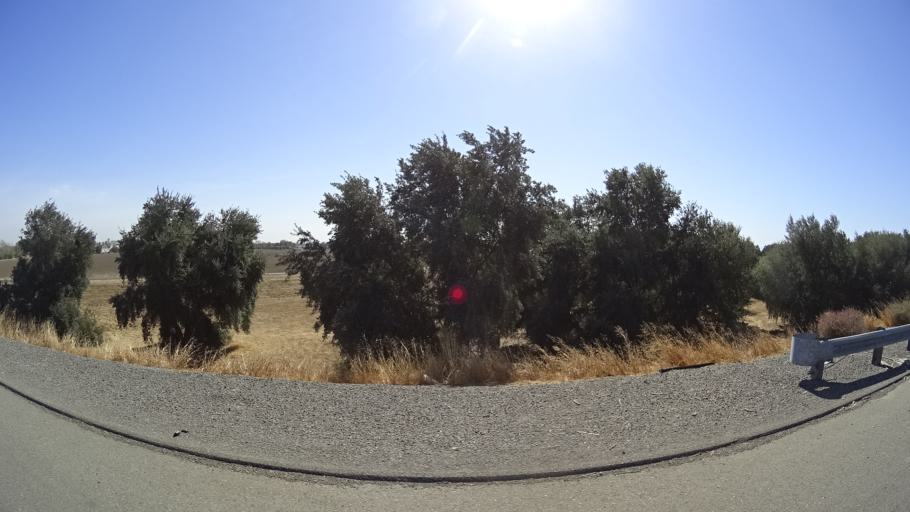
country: US
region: California
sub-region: Yolo County
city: Woodland
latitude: 38.6193
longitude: -121.7657
